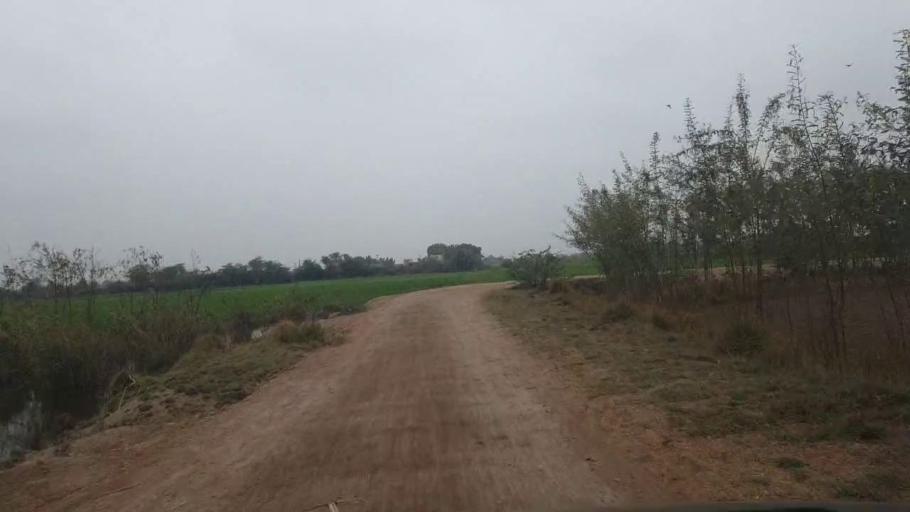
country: PK
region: Sindh
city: Tando Adam
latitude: 25.8428
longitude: 68.7121
